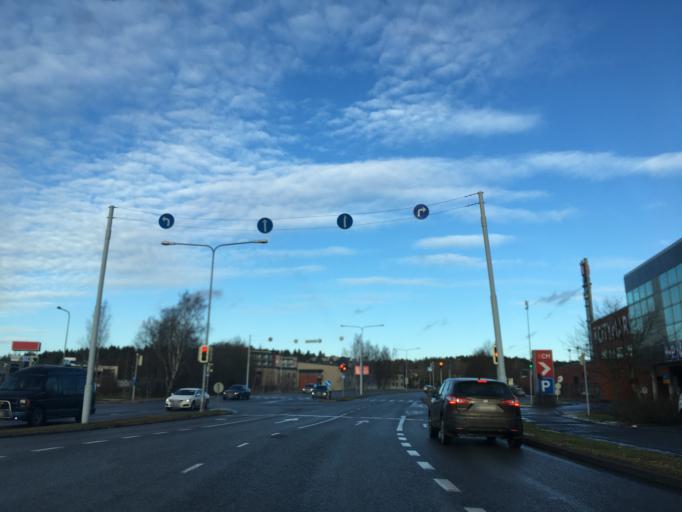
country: FI
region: Varsinais-Suomi
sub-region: Turku
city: Turku
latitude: 60.4723
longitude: 22.2306
